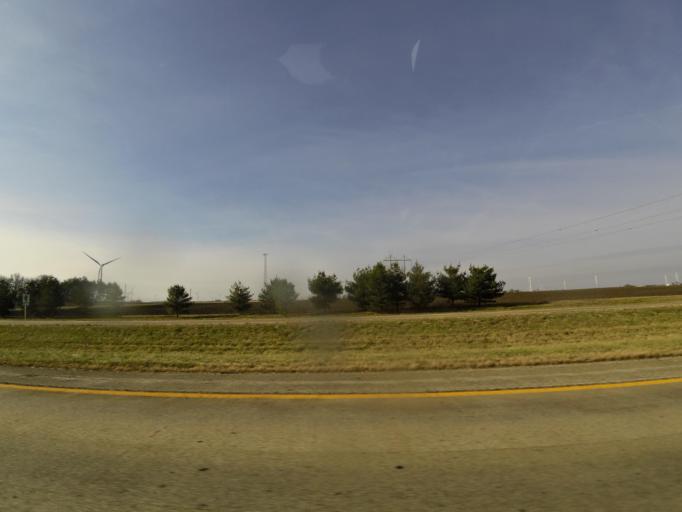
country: US
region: Illinois
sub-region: Macon County
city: Maroa
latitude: 40.0235
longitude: -88.9562
